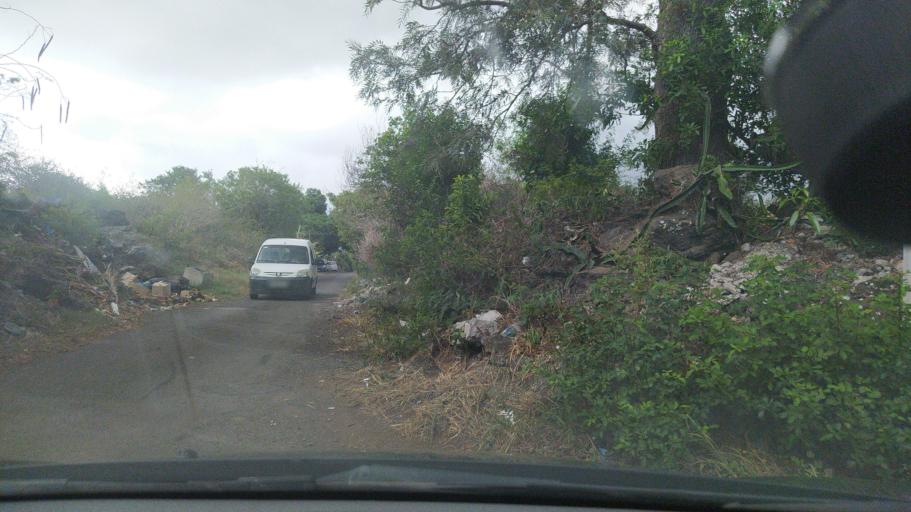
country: RE
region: Reunion
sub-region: Reunion
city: Saint-Pierre
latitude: -21.3046
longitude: 55.4644
